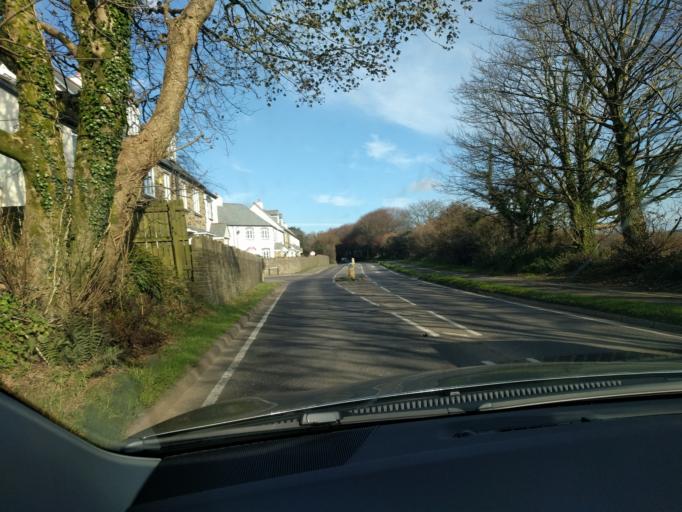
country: GB
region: England
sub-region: Cornwall
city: Camelford
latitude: 50.6152
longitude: -4.6849
